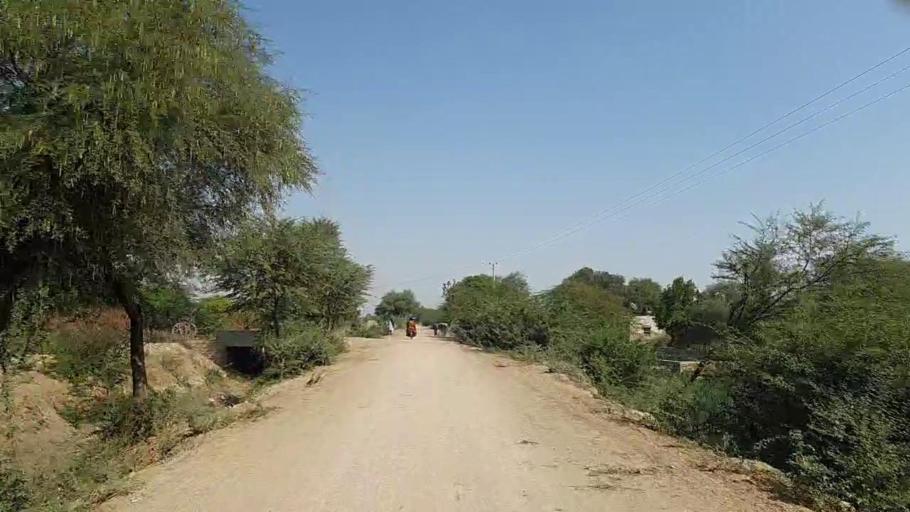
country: PK
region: Sindh
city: Mirpur Batoro
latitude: 24.6909
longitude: 68.2577
